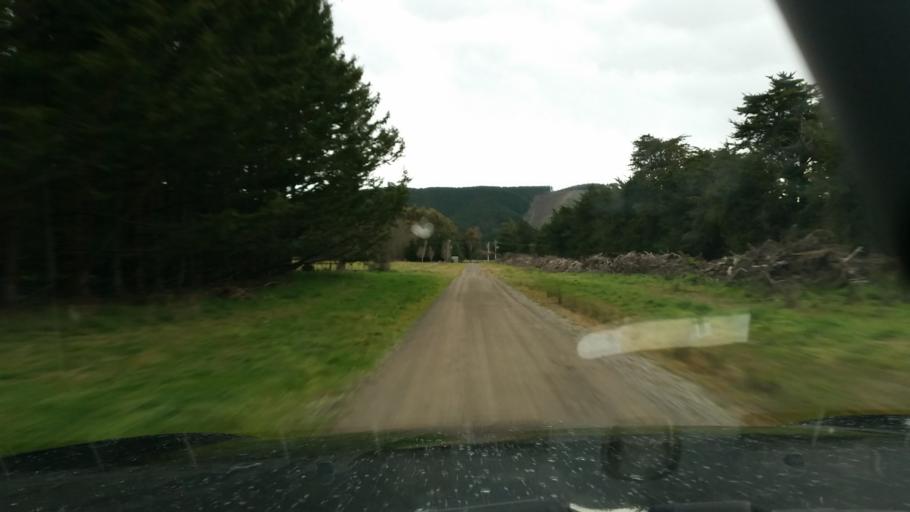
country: NZ
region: Nelson
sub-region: Nelson City
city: Nelson
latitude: -41.5630
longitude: 173.5227
